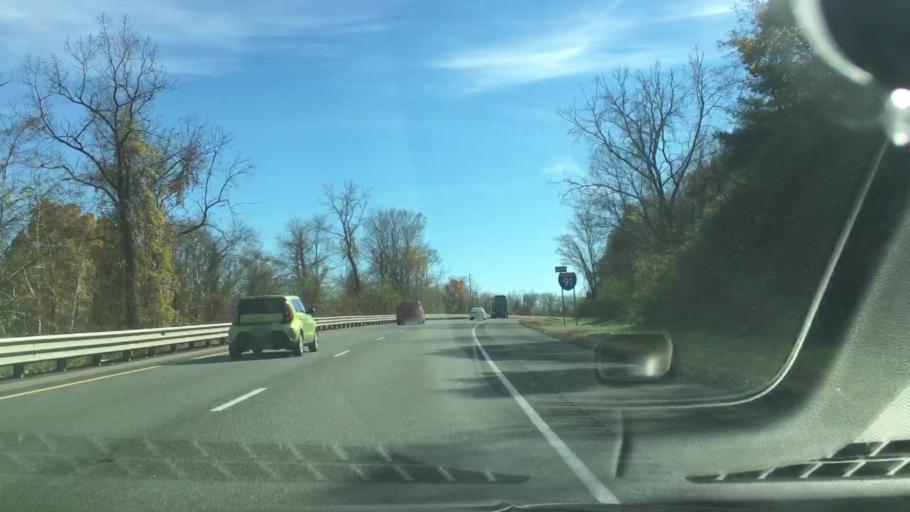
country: US
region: Massachusetts
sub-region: Hampshire County
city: South Hadley
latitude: 42.2801
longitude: -72.6083
